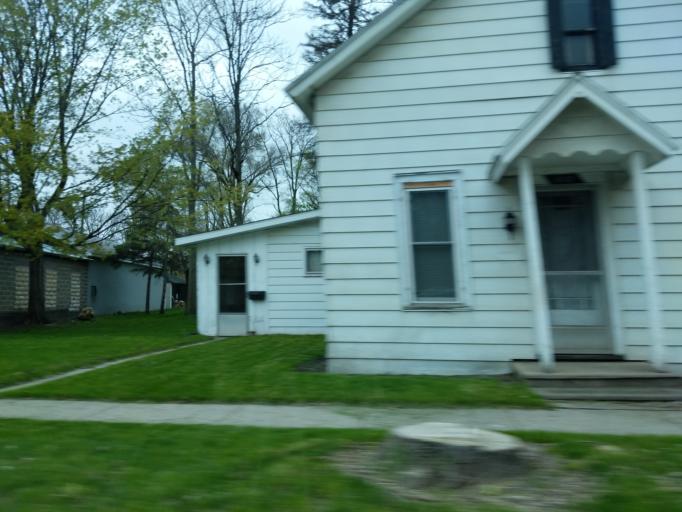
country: US
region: Michigan
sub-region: Tuscola County
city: Vassar
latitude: 43.3699
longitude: -83.5771
